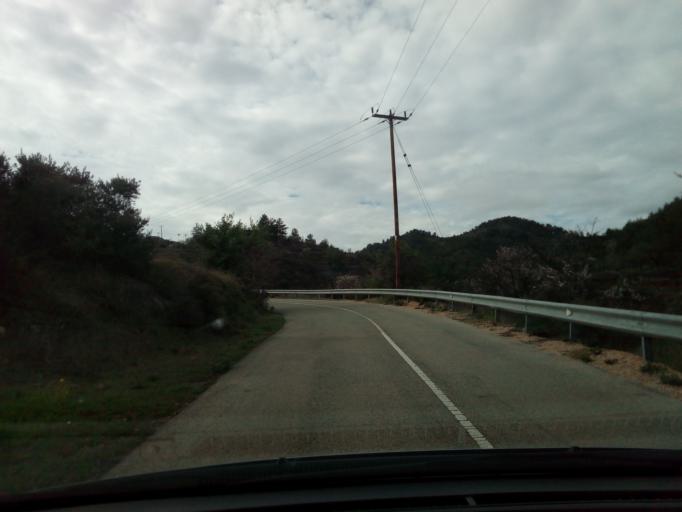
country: CY
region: Lefkosia
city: Klirou
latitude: 34.9761
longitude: 33.1805
